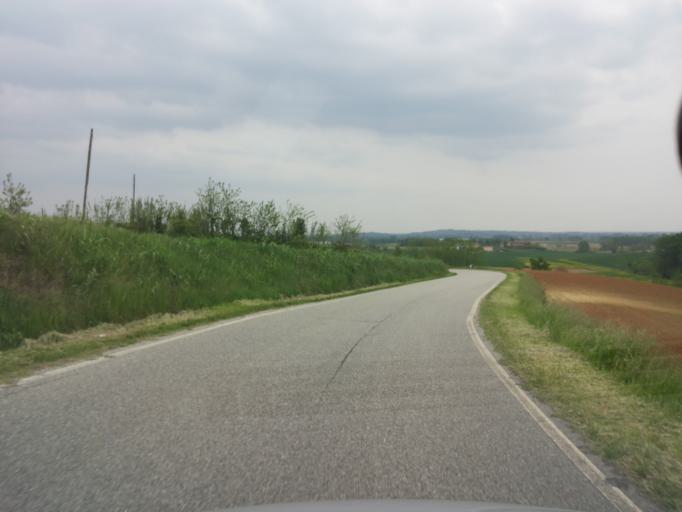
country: IT
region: Piedmont
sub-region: Provincia di Alessandria
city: Mirabello Monferrato
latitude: 45.0160
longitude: 8.5112
